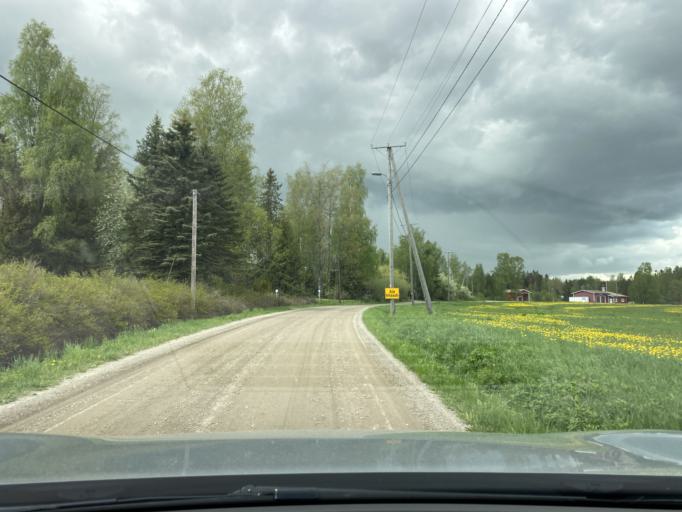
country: FI
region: Uusimaa
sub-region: Porvoo
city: Pukkila
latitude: 60.7562
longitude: 25.4341
